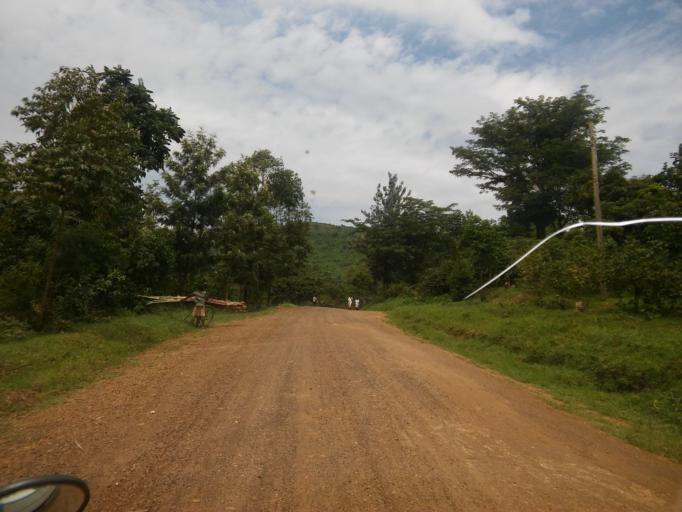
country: UG
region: Eastern Region
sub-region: Bududa District
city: Bududa
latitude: 0.9231
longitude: 34.2811
